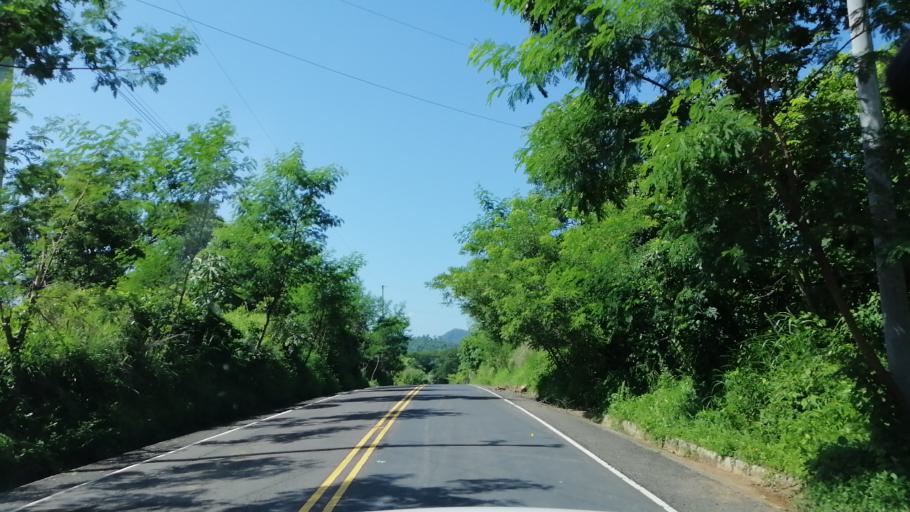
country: HN
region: Lempira
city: La Virtud
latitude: 13.9648
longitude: -88.7646
